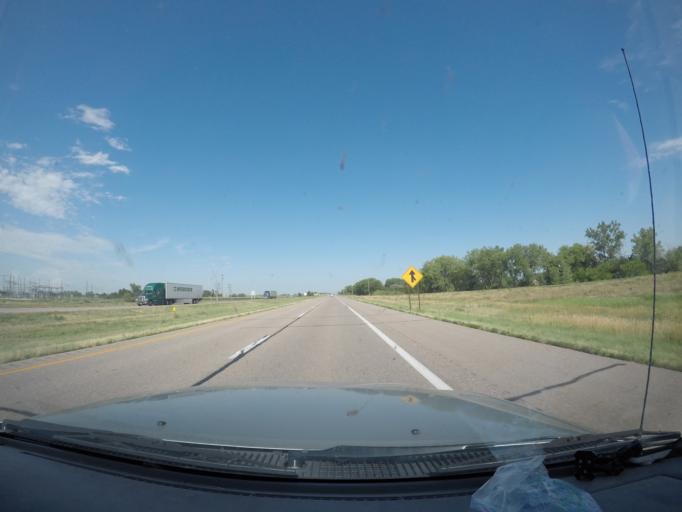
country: US
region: Nebraska
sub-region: Phelps County
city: Holdrege
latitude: 40.6900
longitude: -99.3780
